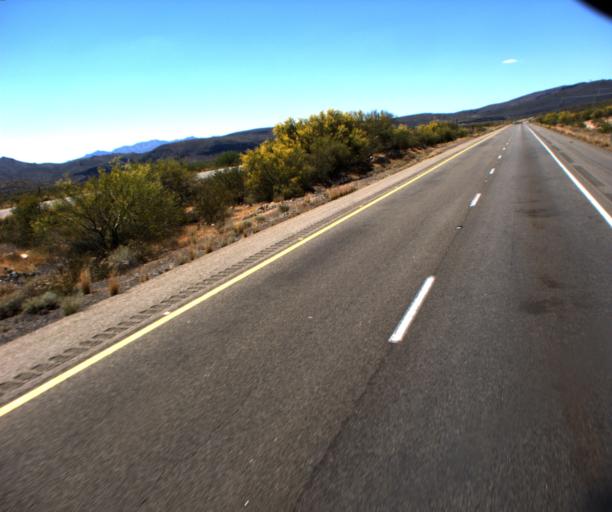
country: US
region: Arizona
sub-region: Yavapai County
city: Bagdad
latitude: 34.5222
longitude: -113.4241
